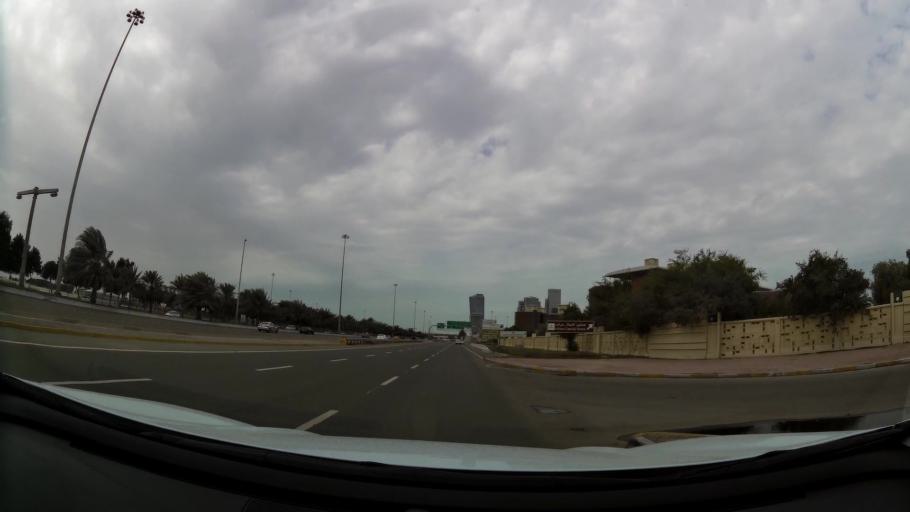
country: AE
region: Abu Dhabi
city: Abu Dhabi
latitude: 24.4141
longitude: 54.4490
